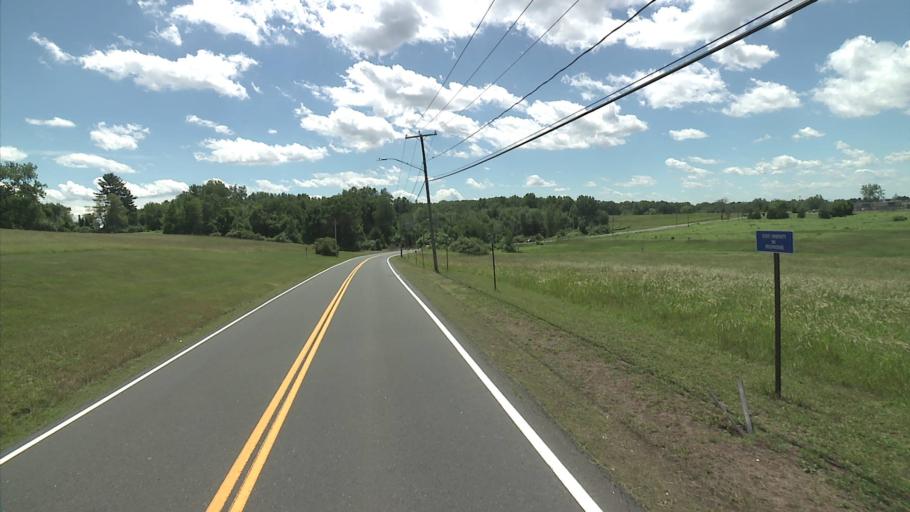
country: US
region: Massachusetts
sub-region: Hampden County
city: East Longmeadow
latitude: 42.0189
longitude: -72.5026
